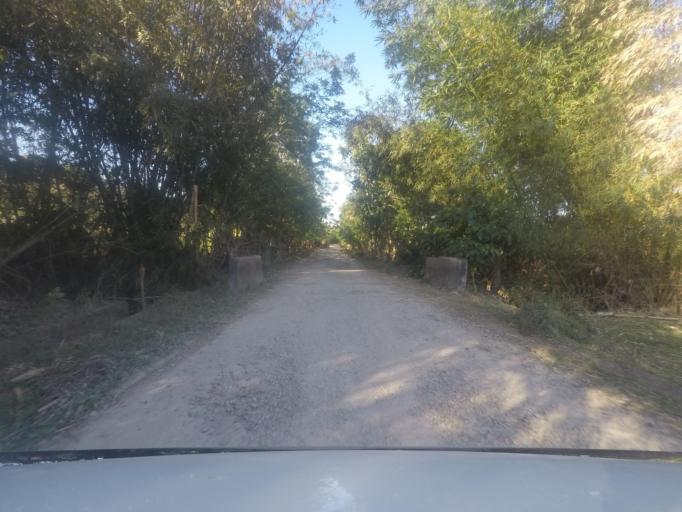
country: TL
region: Lautem
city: Lospalos
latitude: -8.4102
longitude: 127.1585
